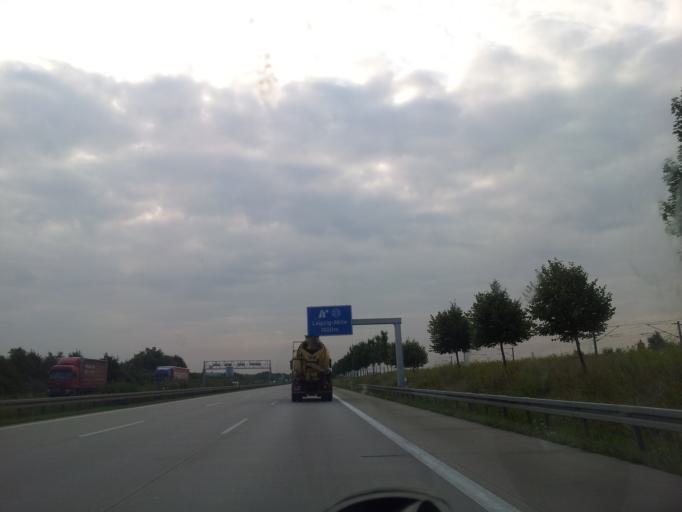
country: DE
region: Saxony
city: Rackwitz
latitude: 51.4100
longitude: 12.3653
